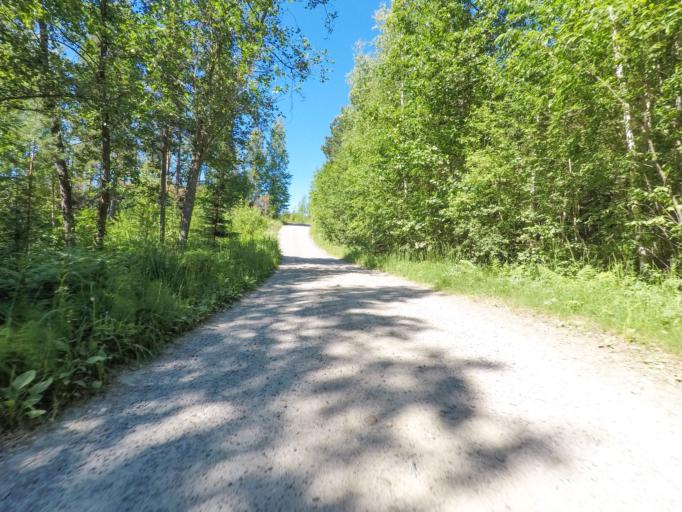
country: FI
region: Northern Savo
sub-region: Varkaus
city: Kangaslampi
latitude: 62.1764
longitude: 28.2370
